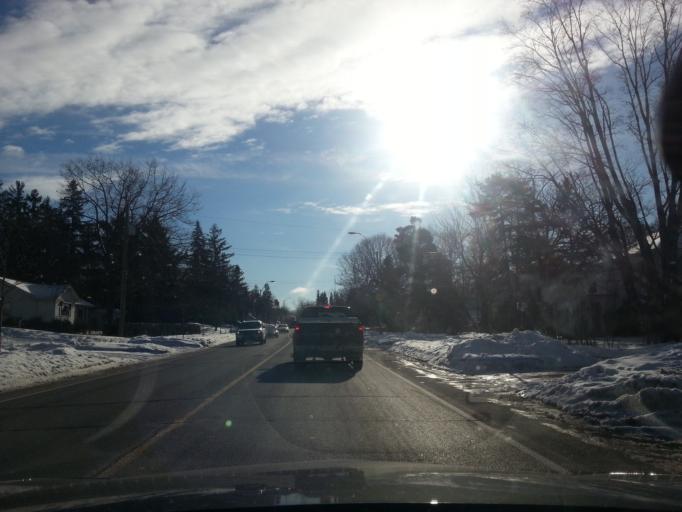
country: CA
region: Ontario
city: Ottawa
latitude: 45.3942
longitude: -75.6628
